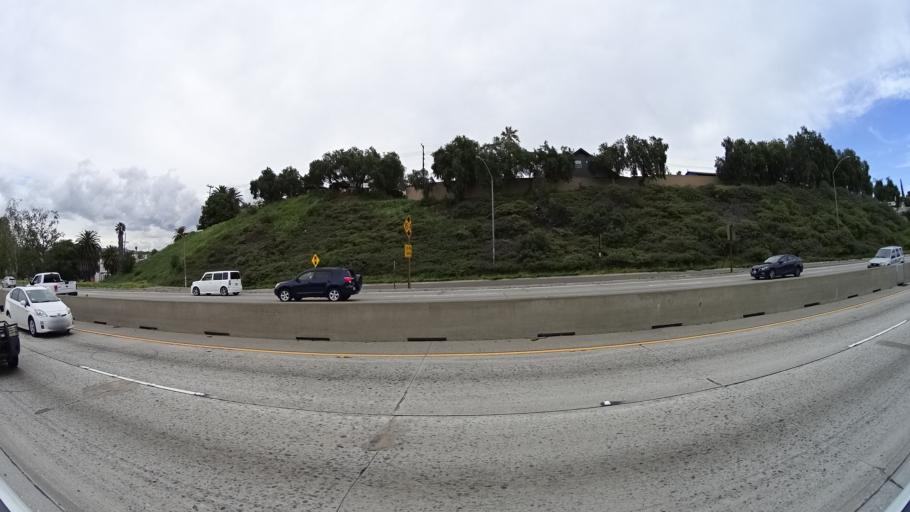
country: US
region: California
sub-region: Los Angeles County
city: Echo Park
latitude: 34.0714
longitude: -118.2655
